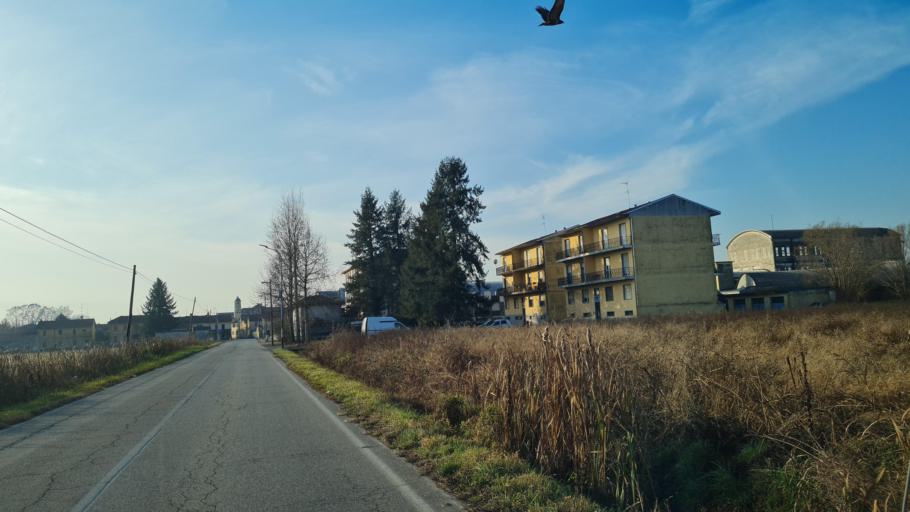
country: IT
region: Piedmont
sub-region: Provincia di Vercelli
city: Albano Vercellese
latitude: 45.4311
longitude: 8.3814
